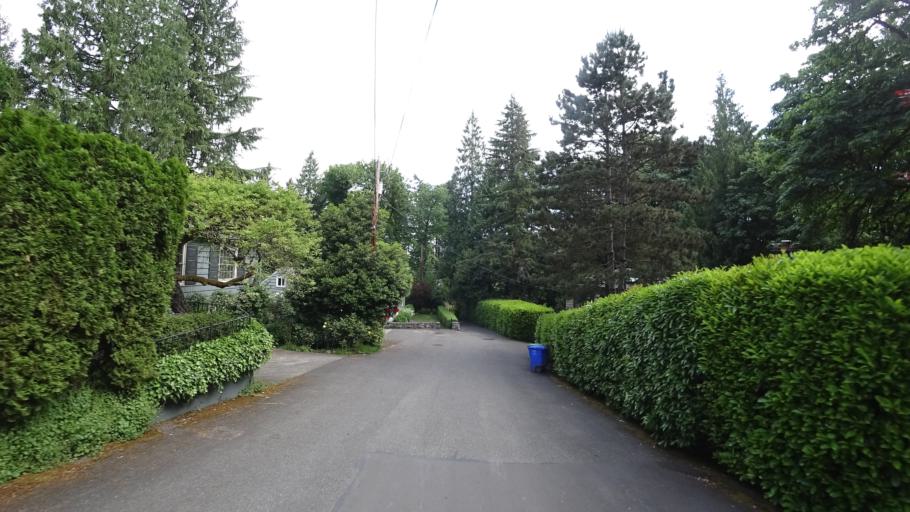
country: US
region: Oregon
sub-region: Multnomah County
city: Portland
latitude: 45.5045
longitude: -122.7104
